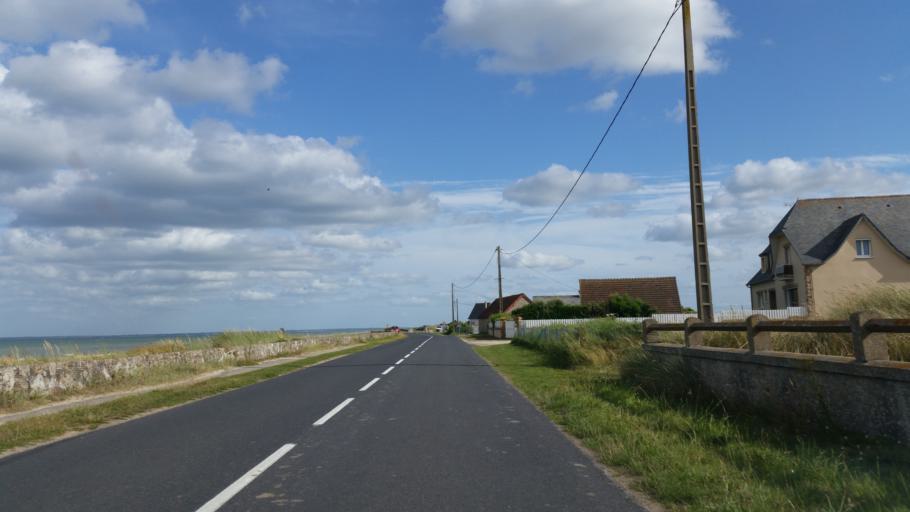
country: FR
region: Lower Normandy
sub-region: Departement de la Manche
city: Sainte-Mere-Eglise
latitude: 49.4555
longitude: -1.2228
